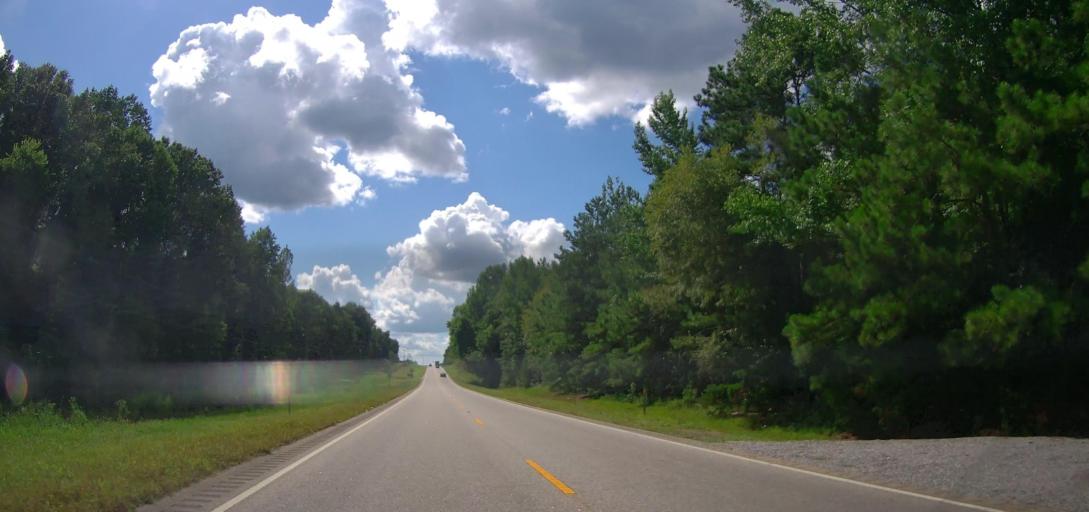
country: US
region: Alabama
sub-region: Macon County
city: Tuskegee
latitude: 32.4612
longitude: -85.5564
